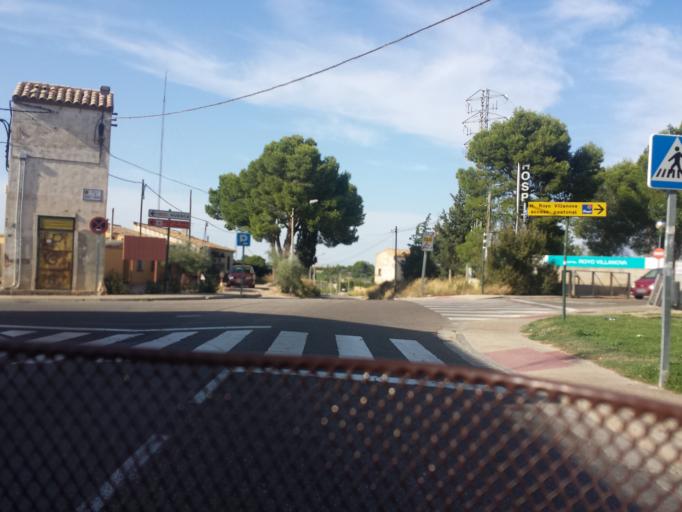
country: ES
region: Aragon
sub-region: Provincia de Zaragoza
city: Zaragoza
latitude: 41.6926
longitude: -0.8623
